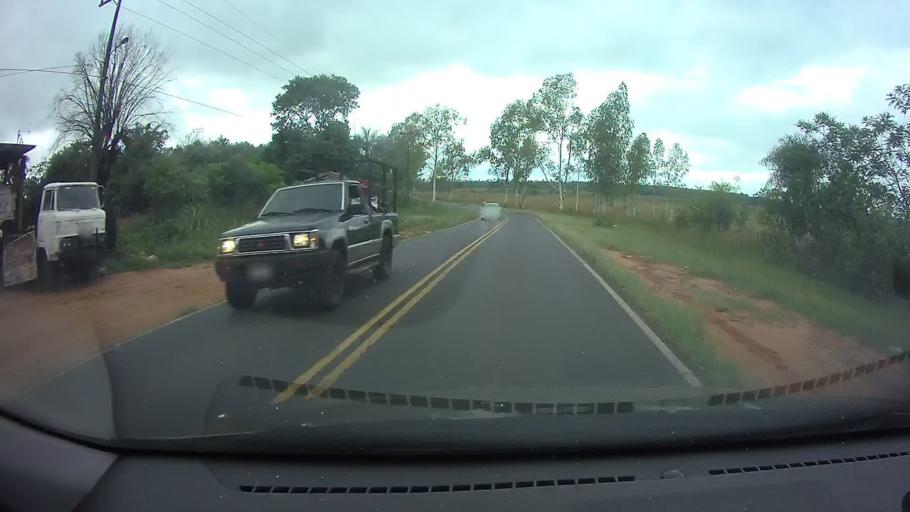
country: PY
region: Central
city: Nueva Italia
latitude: -25.5532
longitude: -57.5025
